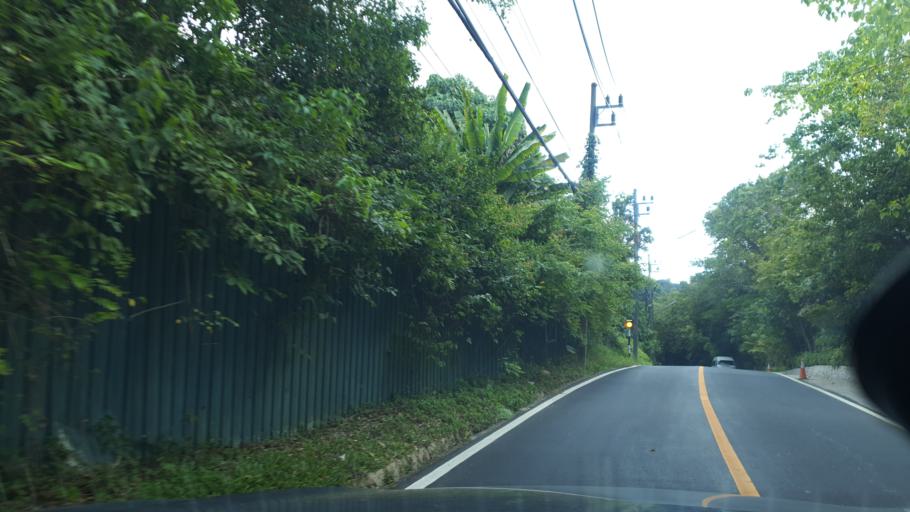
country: TH
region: Phuket
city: Thalang
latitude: 8.0499
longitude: 98.2781
